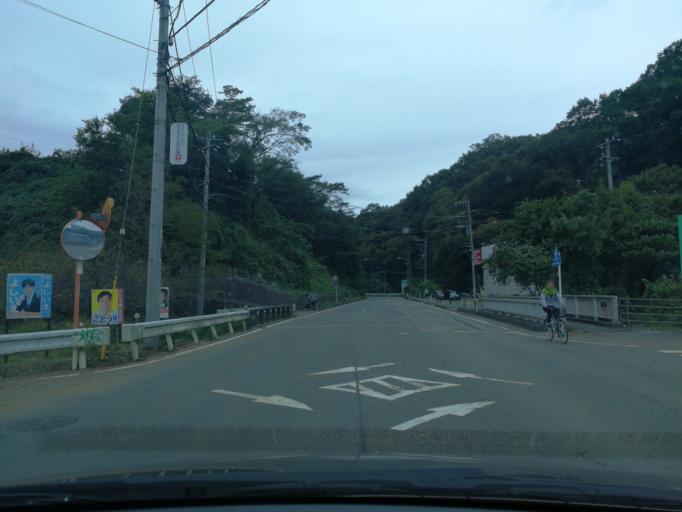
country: JP
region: Yamanashi
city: Uenohara
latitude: 35.5999
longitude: 139.2105
